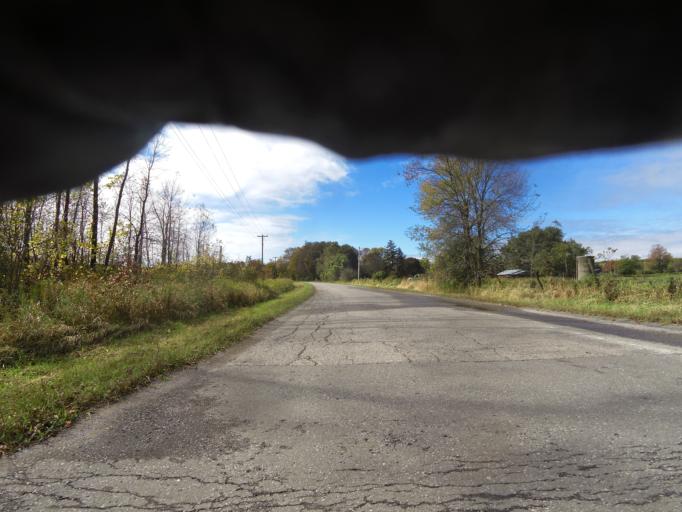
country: CA
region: Ontario
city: Cobourg
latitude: 43.9360
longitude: -78.3745
